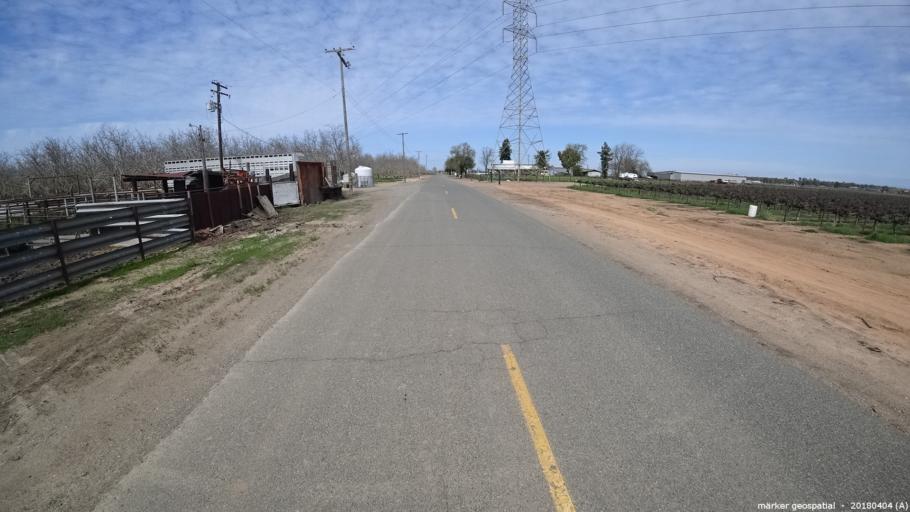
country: US
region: California
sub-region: Sacramento County
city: Herald
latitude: 38.2821
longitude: -121.2082
